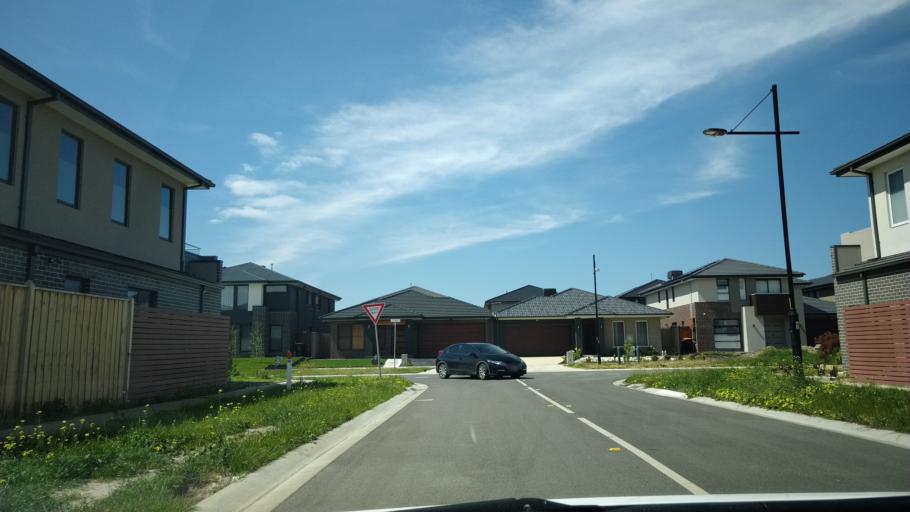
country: AU
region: Victoria
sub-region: Greater Dandenong
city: Keysborough
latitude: -38.0069
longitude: 145.1653
